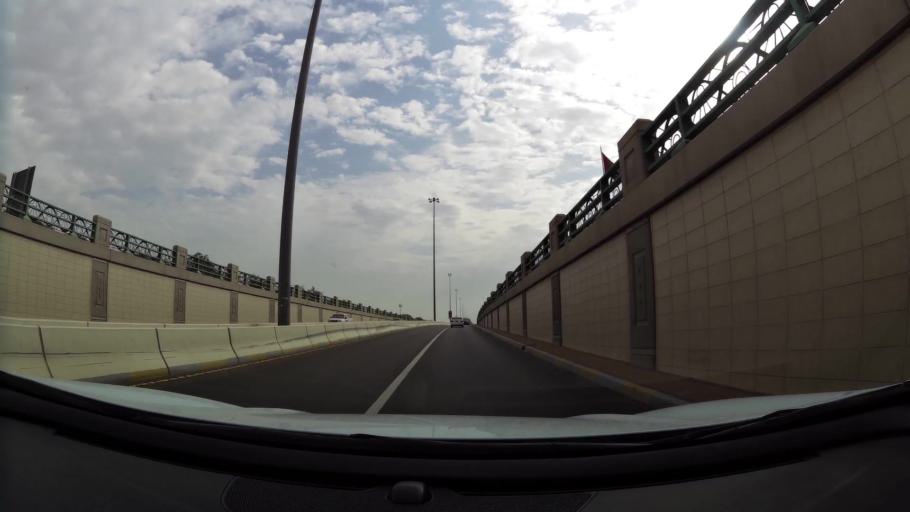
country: AE
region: Abu Dhabi
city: Al Ain
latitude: 24.2236
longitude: 55.7241
